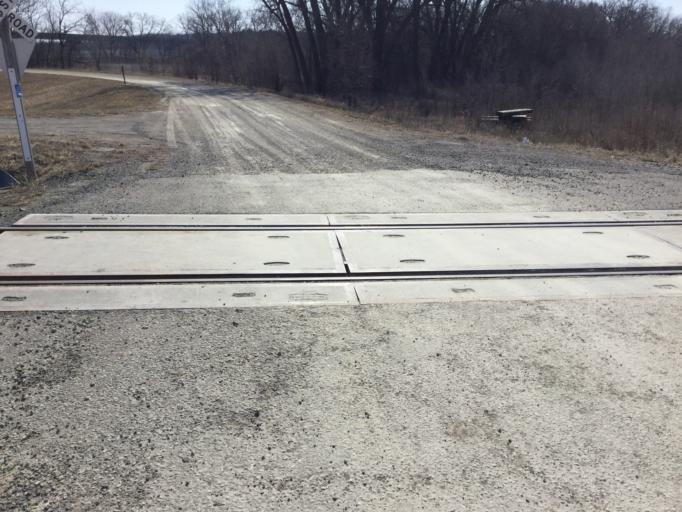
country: US
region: Kansas
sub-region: Marshall County
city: Marysville
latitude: 39.8334
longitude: -96.6491
